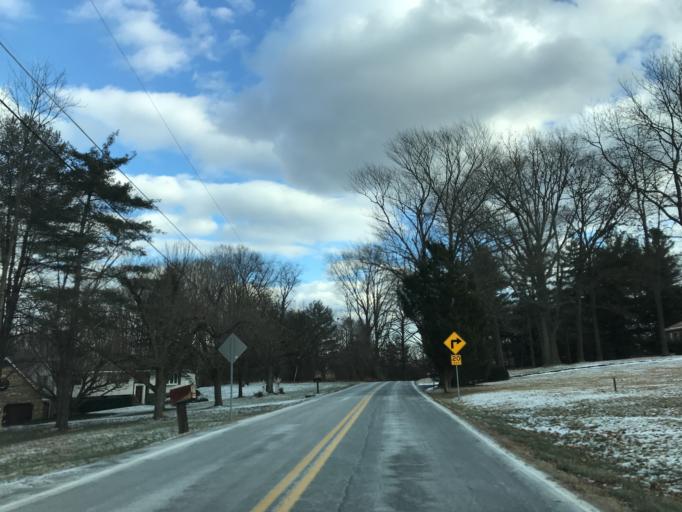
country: US
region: Maryland
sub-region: Harford County
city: Bel Air North
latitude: 39.6387
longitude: -76.3789
